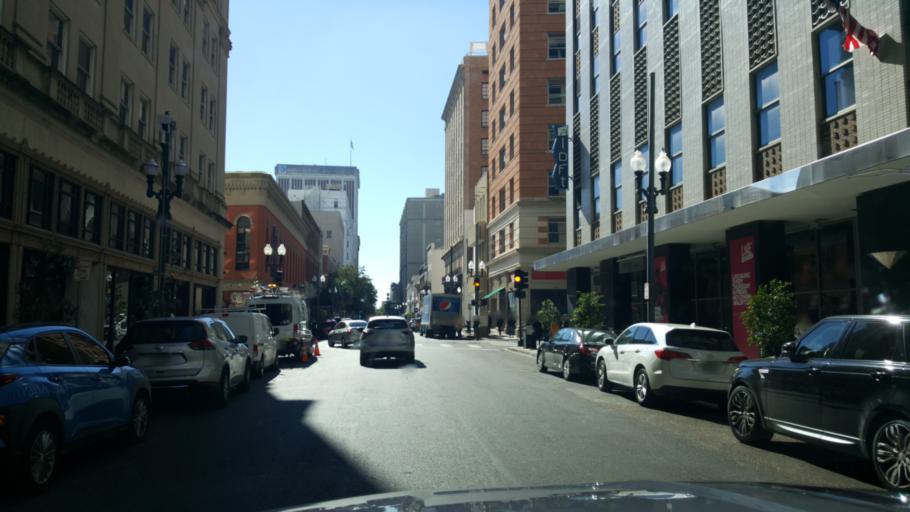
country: US
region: Louisiana
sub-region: Orleans Parish
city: New Orleans
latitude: 29.9531
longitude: -90.0721
